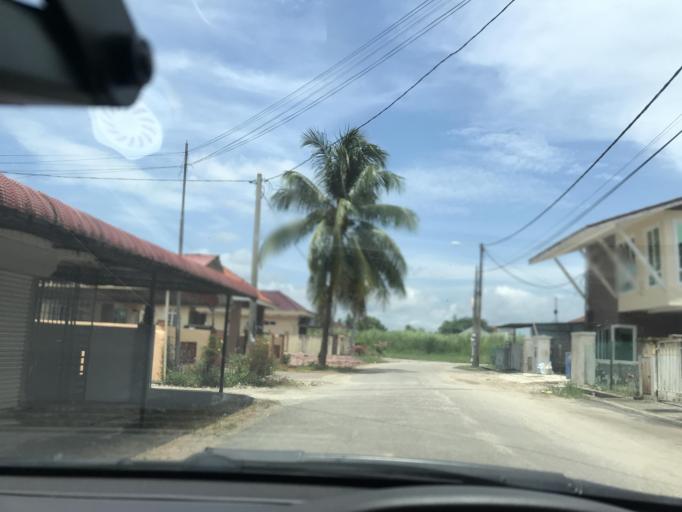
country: MY
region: Kelantan
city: Kota Bharu
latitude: 6.1213
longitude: 102.2193
